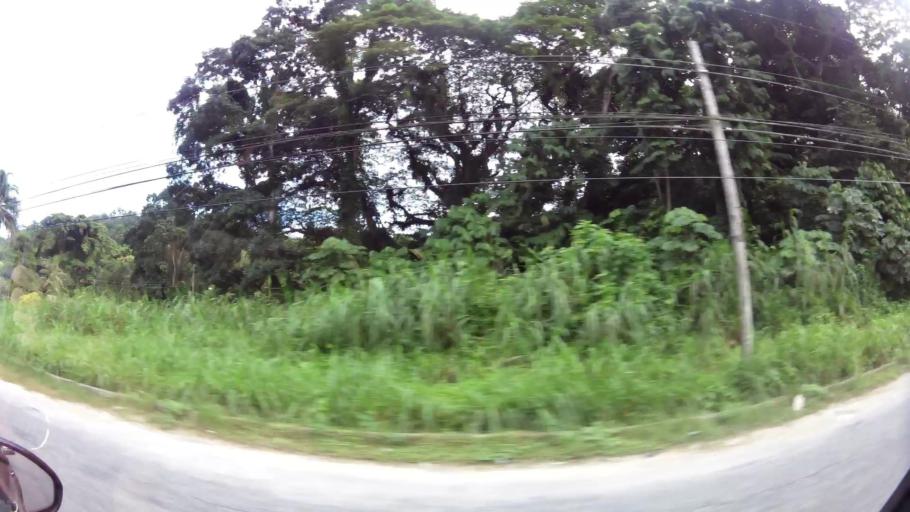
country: TT
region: San Juan/Laventille
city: Laventille
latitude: 10.6994
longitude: -61.4574
